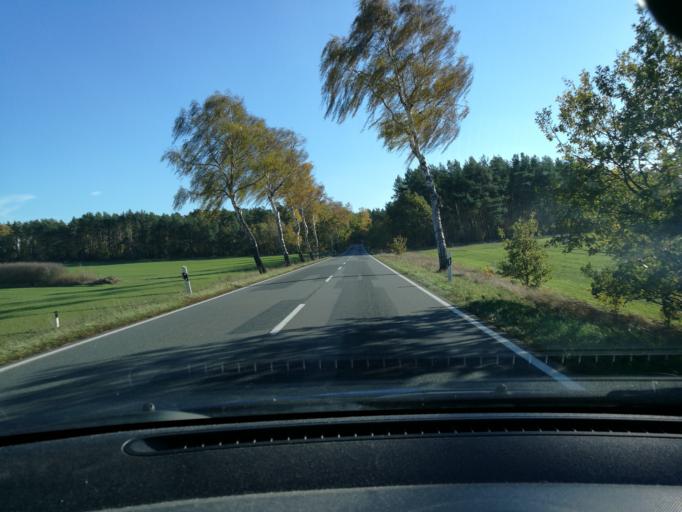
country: DE
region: Lower Saxony
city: Boitze
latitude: 53.1741
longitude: 10.7726
